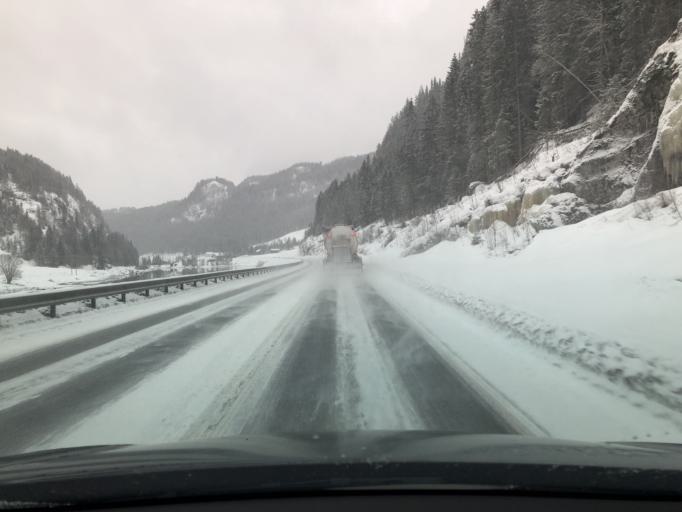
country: NO
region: Oppland
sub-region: Sor-Aurdal
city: Bagn
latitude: 60.7896
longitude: 9.5926
